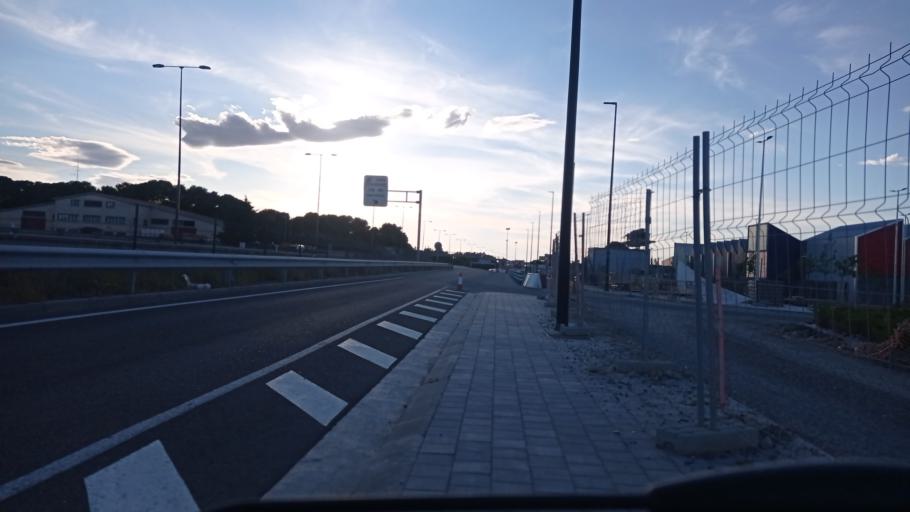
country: ES
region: Aragon
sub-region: Provincia de Zaragoza
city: Oliver-Valdefierro, Oliver, Valdefierro
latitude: 41.6748
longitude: -0.9542
